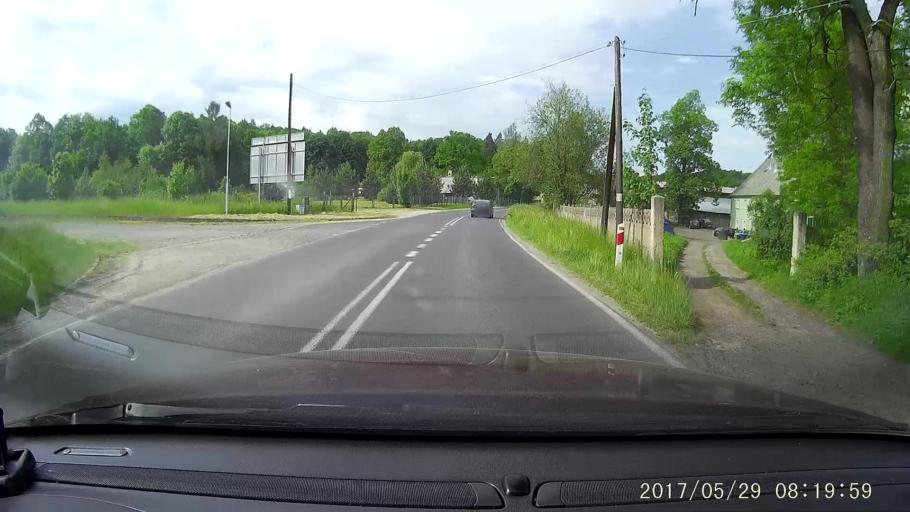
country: PL
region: Lower Silesian Voivodeship
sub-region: Powiat zlotoryjski
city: Zlotoryja
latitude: 51.0986
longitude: 15.8787
